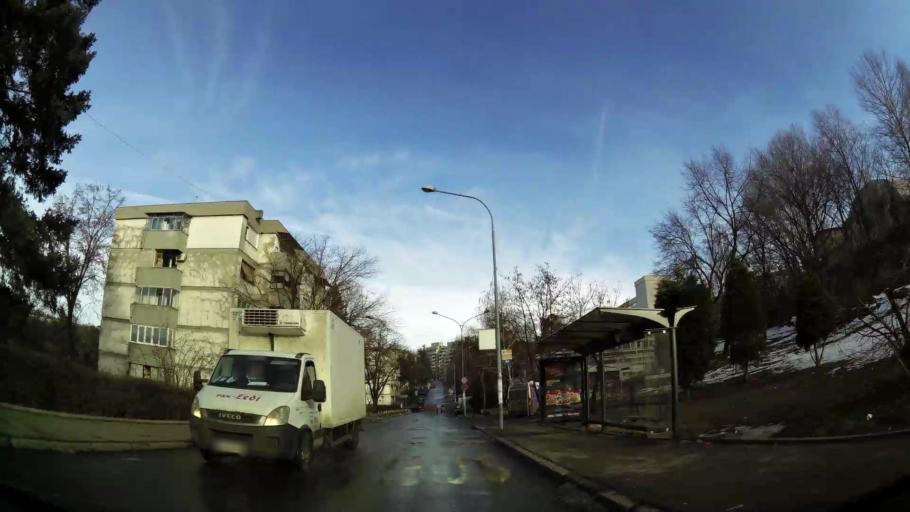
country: RS
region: Central Serbia
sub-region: Belgrade
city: Rakovica
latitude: 44.7547
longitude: 20.4539
